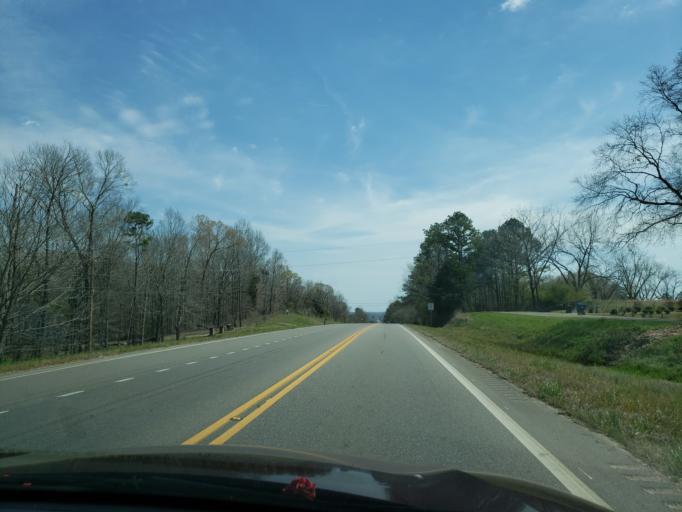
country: US
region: Alabama
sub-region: Autauga County
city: Prattville
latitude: 32.4305
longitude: -86.5361
